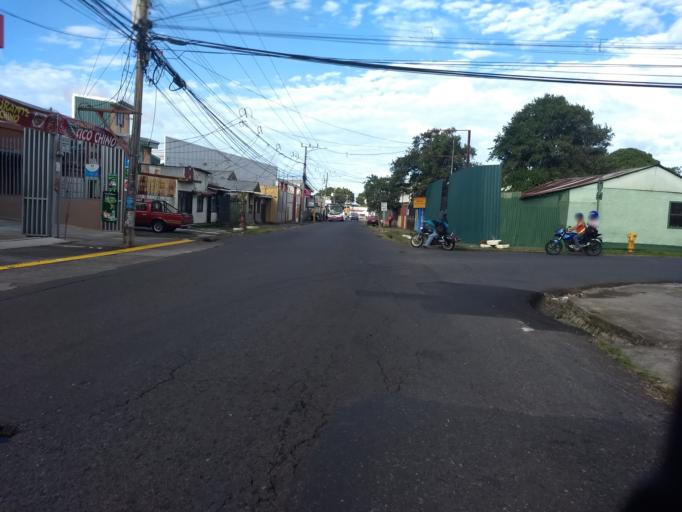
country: CR
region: San Jose
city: San Juan
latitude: 9.9556
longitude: -84.0836
